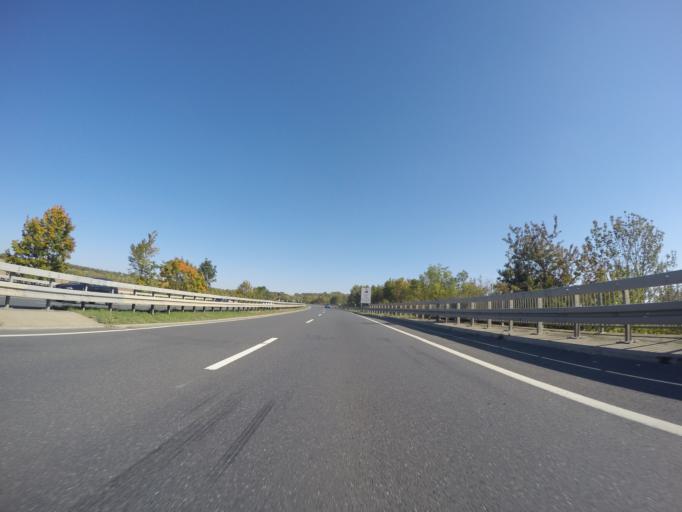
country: DE
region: Bavaria
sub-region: Regierungsbezirk Unterfranken
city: Estenfeld
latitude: 49.8419
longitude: 10.0066
